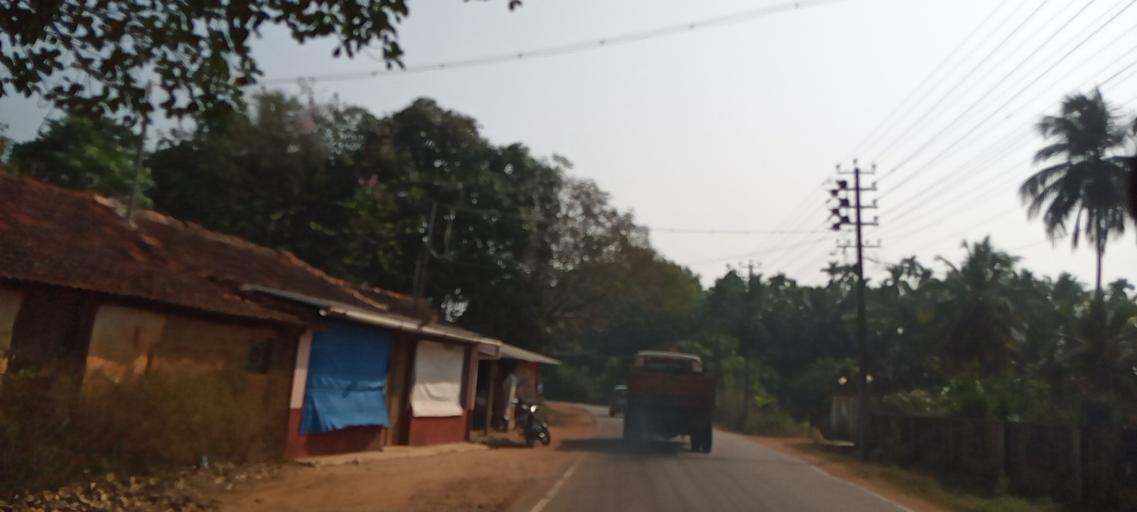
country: IN
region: Karnataka
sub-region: Udupi
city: Coondapoor
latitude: 13.5123
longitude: 74.7375
